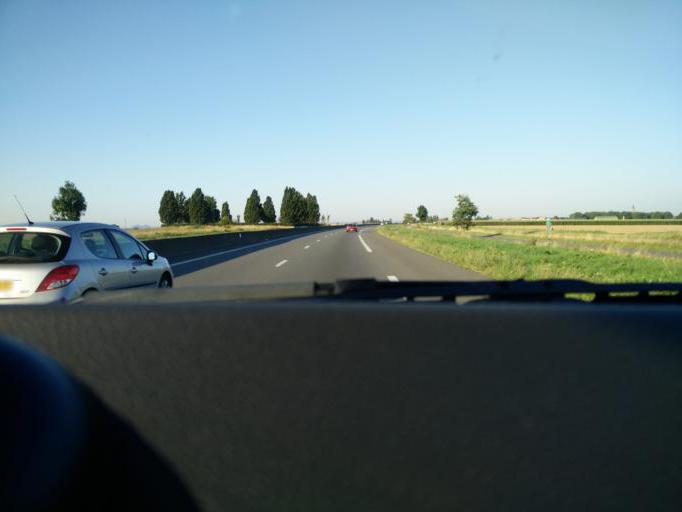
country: FR
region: Nord-Pas-de-Calais
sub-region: Departement du Nord
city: Herlies
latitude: 50.5667
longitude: 2.8515
